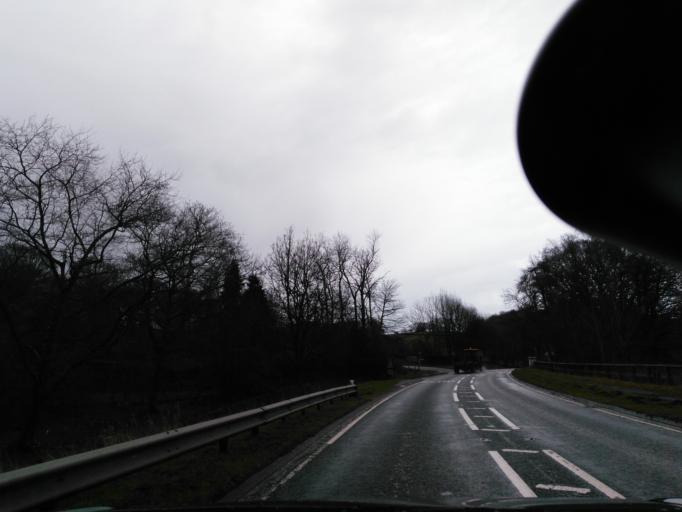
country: GB
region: England
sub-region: Bradford
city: Burley in Wharfedale
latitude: 53.9940
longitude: -1.7430
